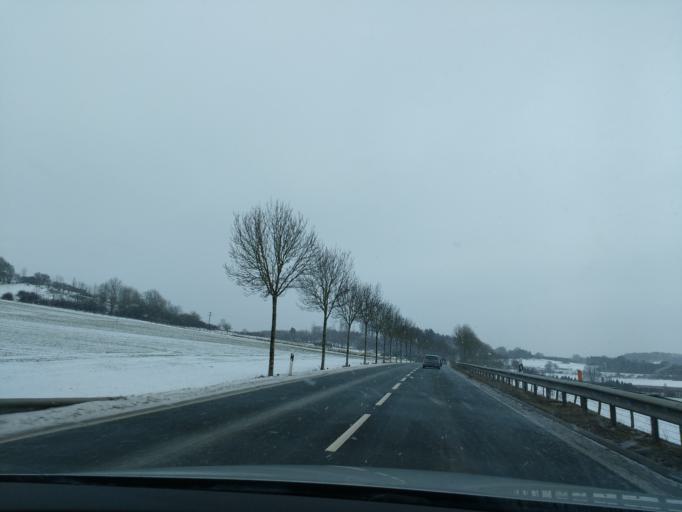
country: DE
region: North Rhine-Westphalia
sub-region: Regierungsbezirk Arnsberg
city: Brilon
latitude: 51.4013
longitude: 8.5993
